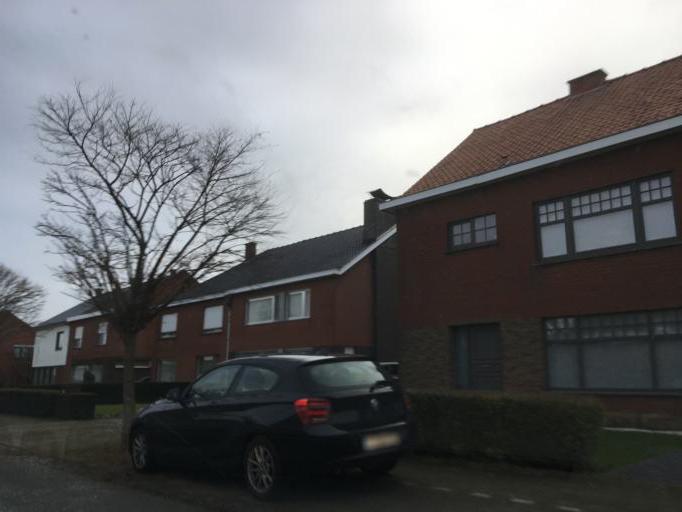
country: BE
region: Flanders
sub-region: Provincie West-Vlaanderen
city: Roeselare
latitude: 50.9581
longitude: 3.1155
